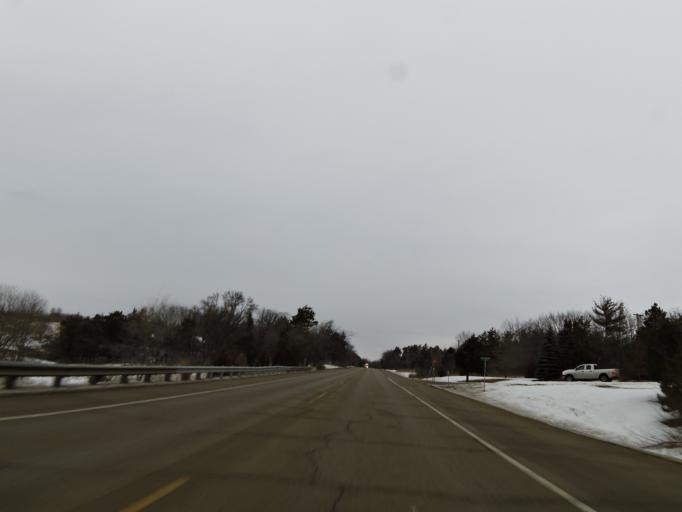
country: US
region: Wisconsin
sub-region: Saint Croix County
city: Hudson
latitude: 44.9744
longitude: -92.7750
